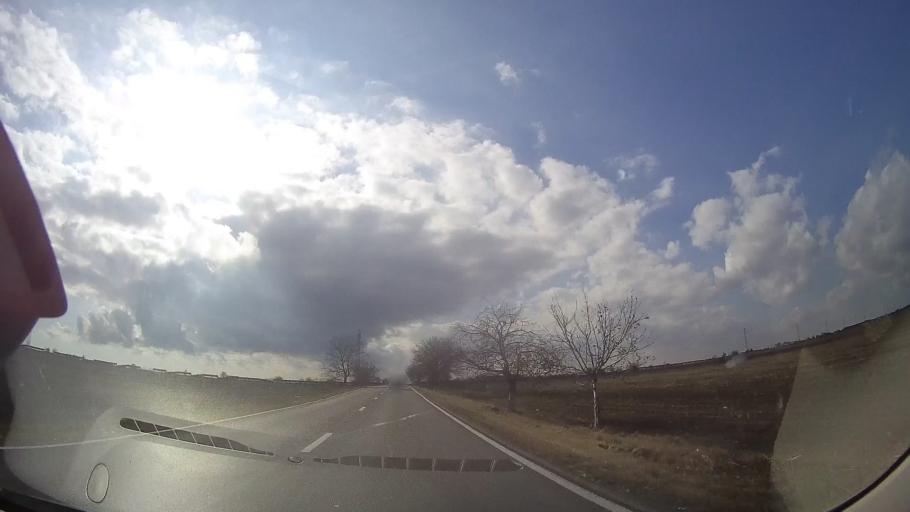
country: RO
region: Constanta
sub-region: Comuna Agigea
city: Agigea
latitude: 44.0748
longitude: 28.5992
